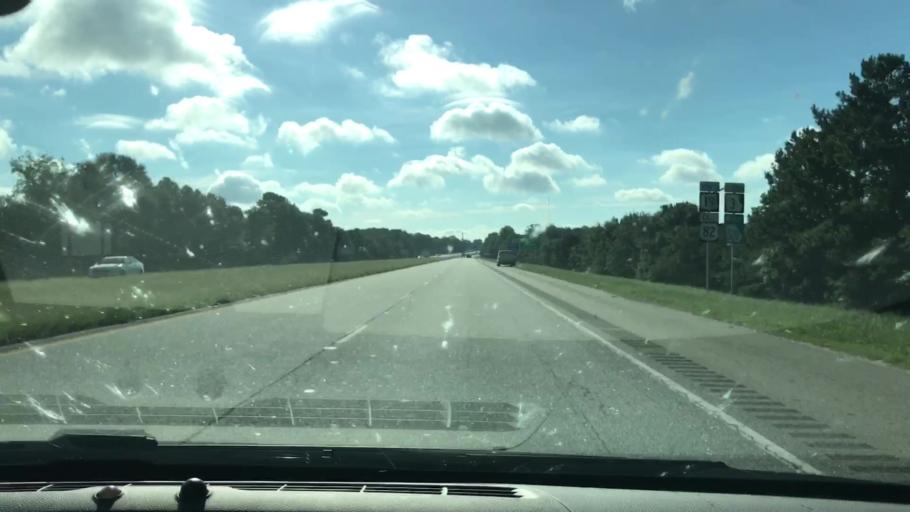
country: US
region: Georgia
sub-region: Dougherty County
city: Albany
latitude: 31.6138
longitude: -84.1692
